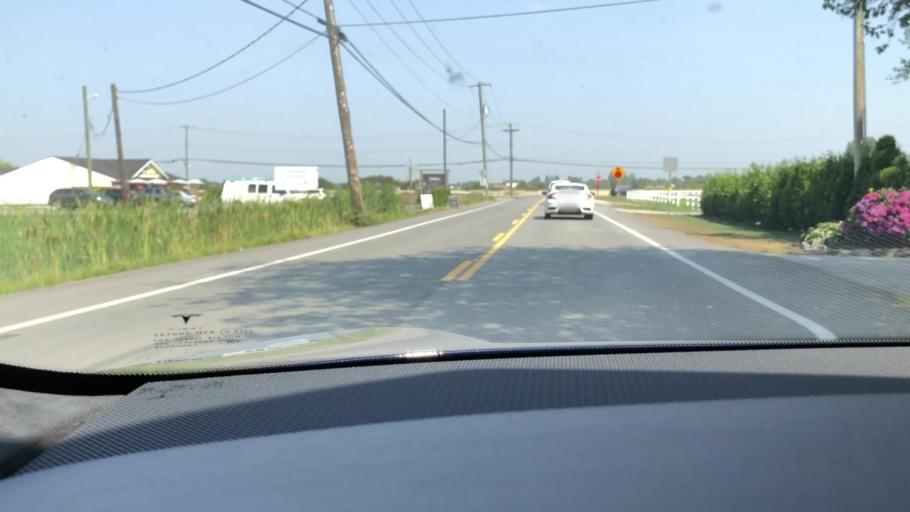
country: CA
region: British Columbia
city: Ladner
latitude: 49.0528
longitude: -123.0797
